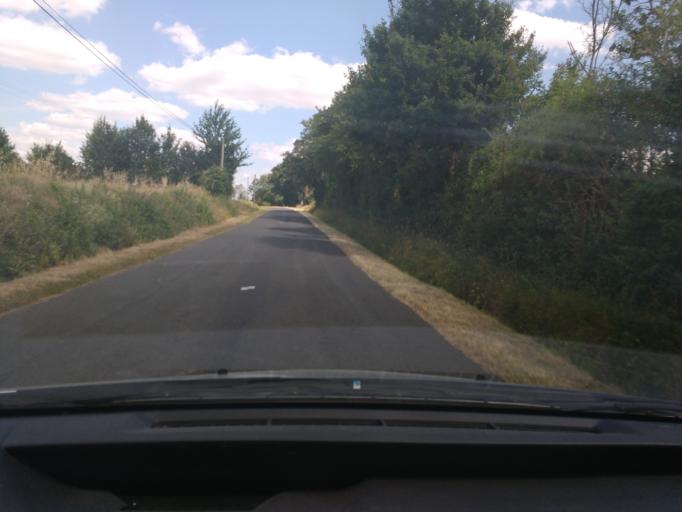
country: FR
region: Pays de la Loire
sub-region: Departement de Maine-et-Loire
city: Bauge-en-Anjou
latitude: 47.5466
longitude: -0.0472
